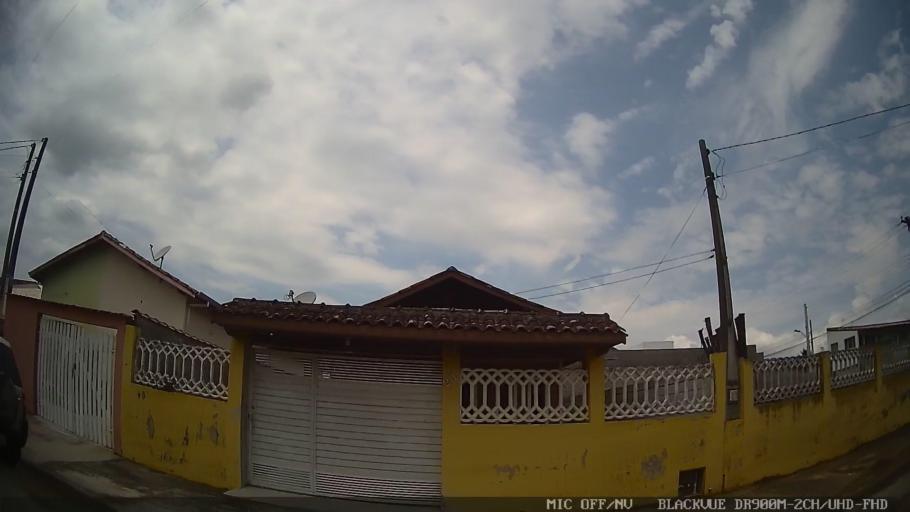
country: BR
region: Sao Paulo
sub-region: Caraguatatuba
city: Caraguatatuba
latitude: -23.6679
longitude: -45.4423
